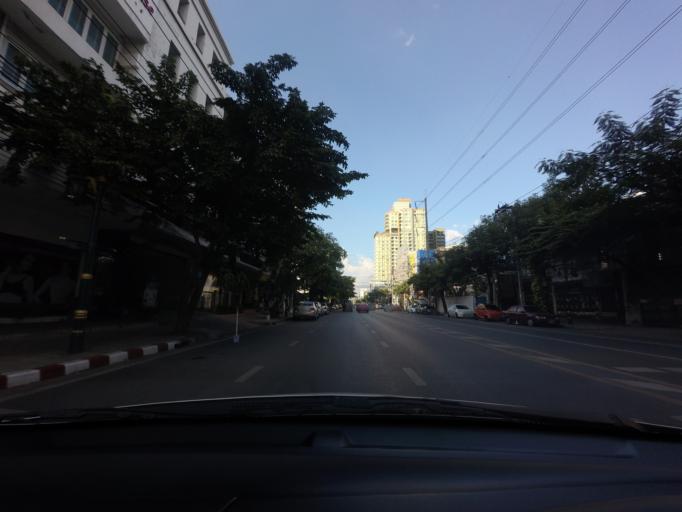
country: TH
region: Bangkok
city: Watthana
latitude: 13.7377
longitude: 100.5838
